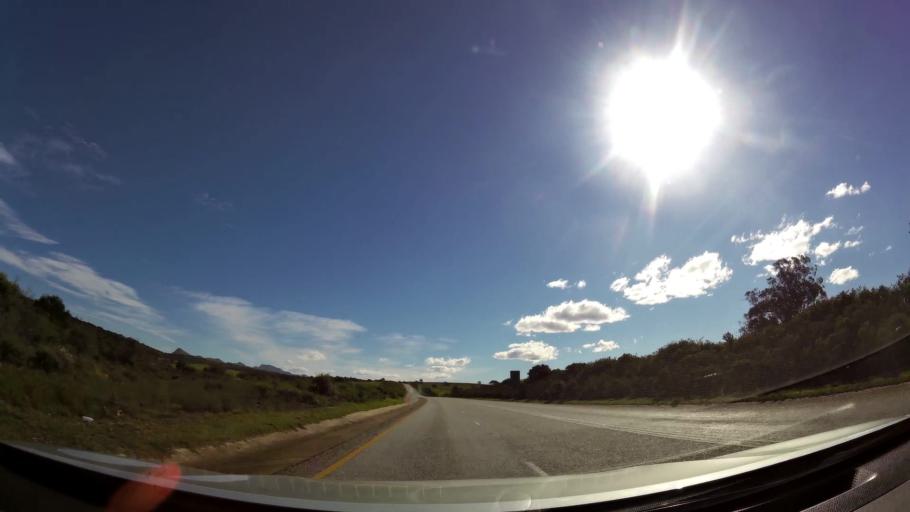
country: ZA
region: Eastern Cape
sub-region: Cacadu District Municipality
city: Kruisfontein
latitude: -34.0360
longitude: 24.5707
